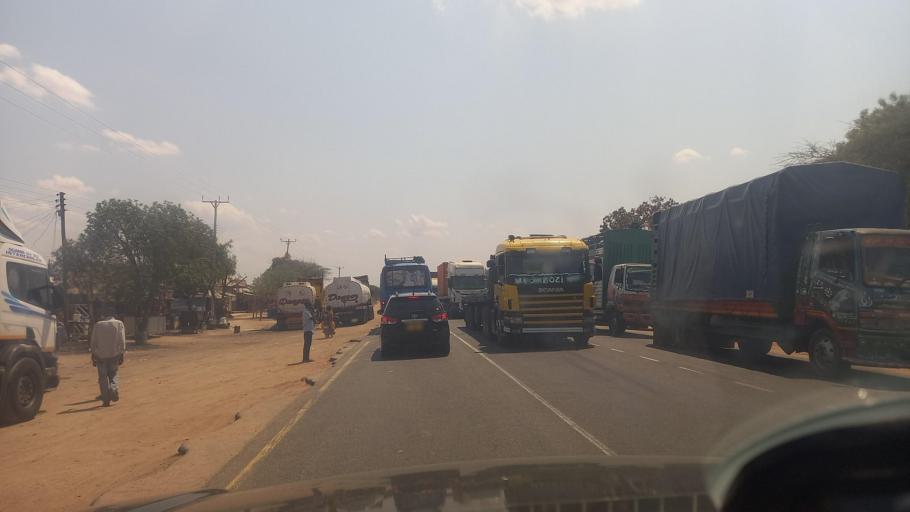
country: TZ
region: Dodoma
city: Msanga
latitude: -6.1423
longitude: 36.0726
